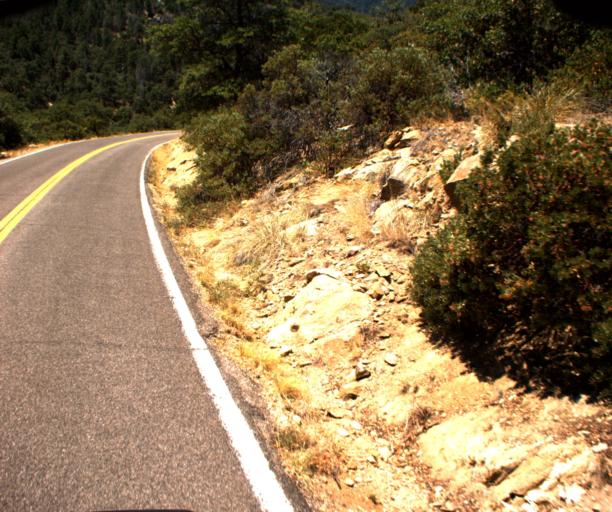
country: US
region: Arizona
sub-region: Graham County
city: Swift Trail Junction
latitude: 32.6532
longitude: -109.8092
